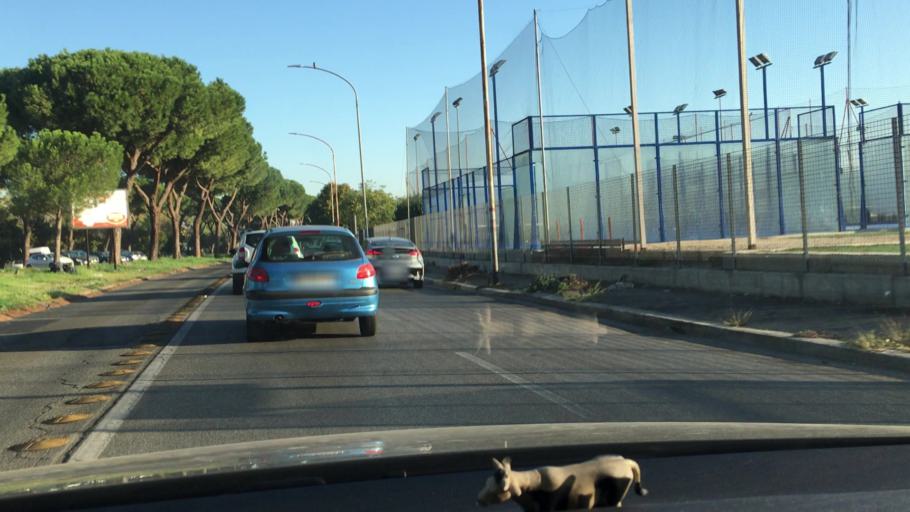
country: IT
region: Latium
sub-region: Citta metropolitana di Roma Capitale
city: Rome
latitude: 41.8708
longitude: 12.5686
